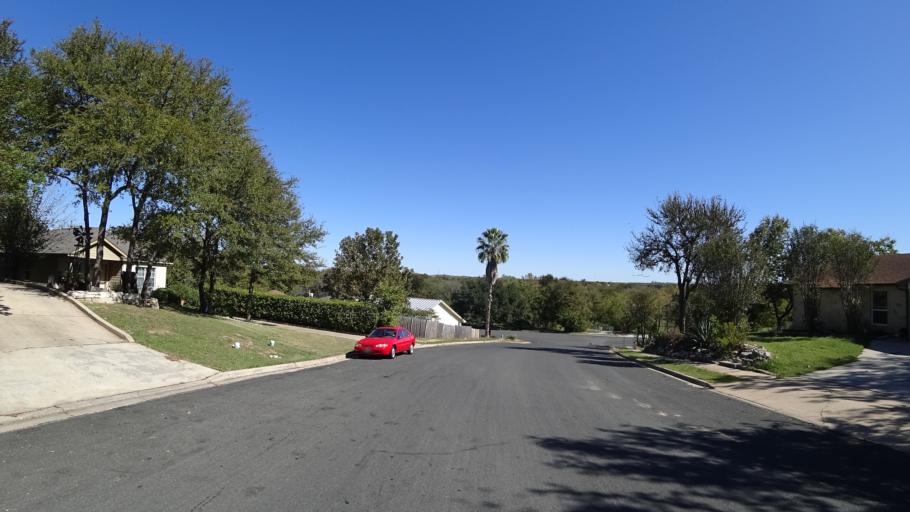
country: US
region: Texas
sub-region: Travis County
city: Hornsby Bend
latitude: 30.2896
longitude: -97.6591
